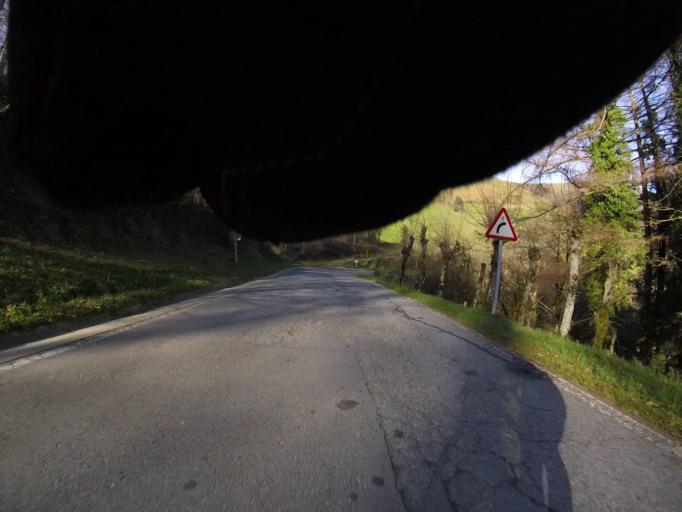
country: ES
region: Navarre
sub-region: Provincia de Navarra
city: Leitza
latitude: 43.0867
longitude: -1.8810
